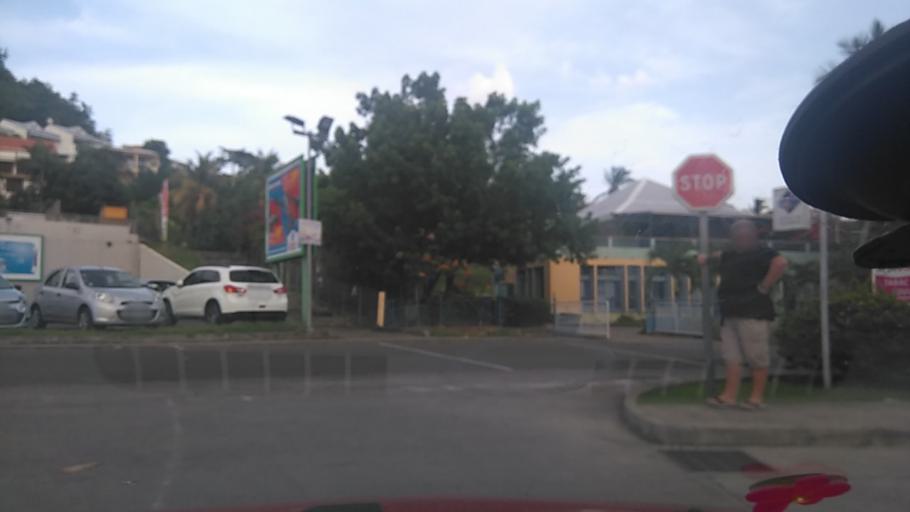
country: MQ
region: Martinique
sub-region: Martinique
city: Le Marin
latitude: 14.4690
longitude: -60.8637
